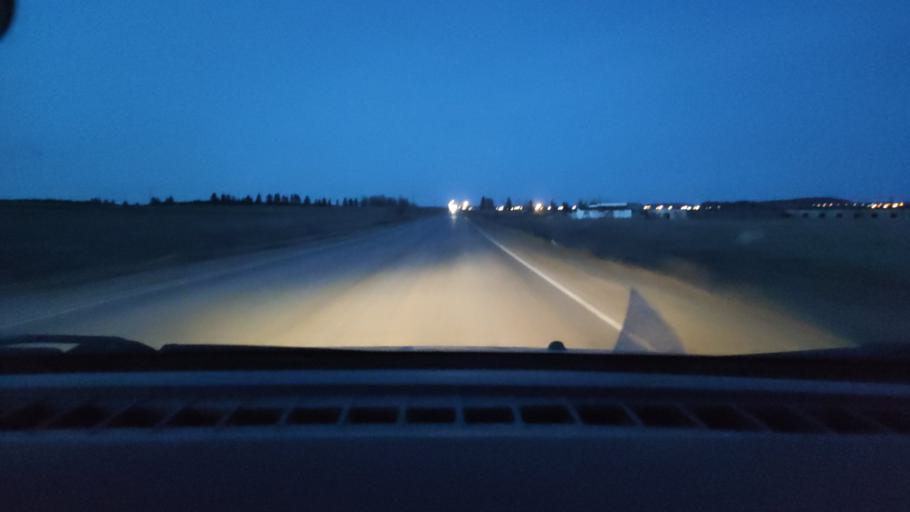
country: RU
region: Perm
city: Lobanovo
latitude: 57.8051
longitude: 56.2908
